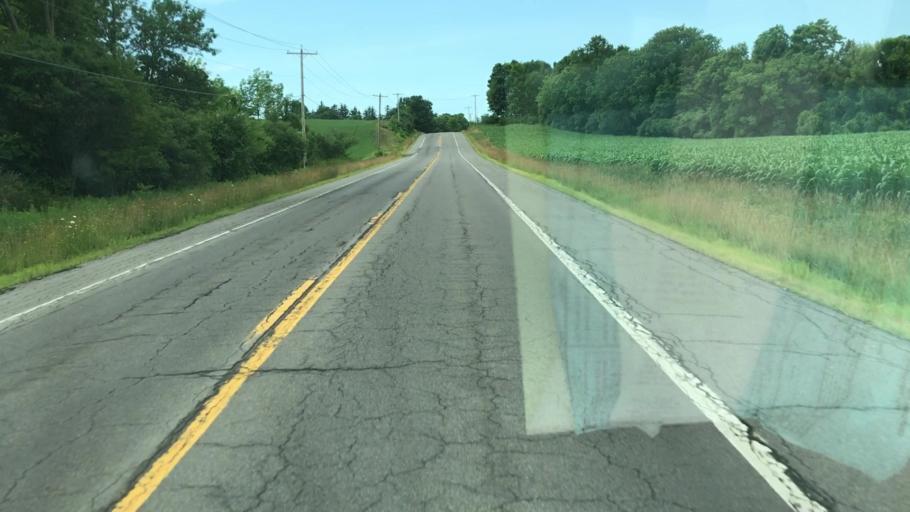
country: US
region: New York
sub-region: Onondaga County
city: Skaneateles
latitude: 42.9405
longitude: -76.3809
